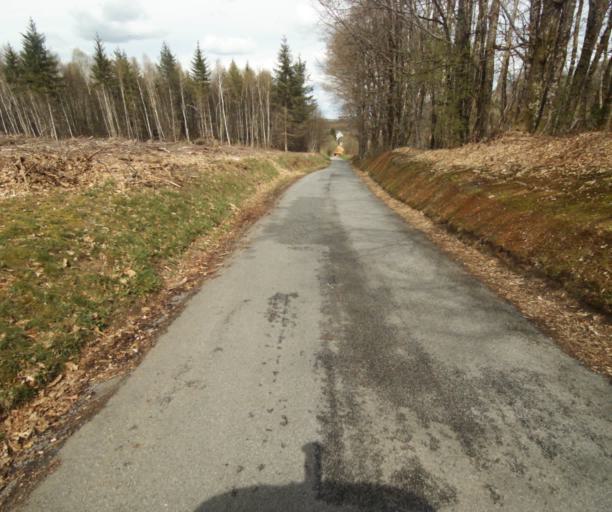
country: FR
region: Limousin
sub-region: Departement de la Correze
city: Laguenne
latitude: 45.2153
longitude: 1.8926
